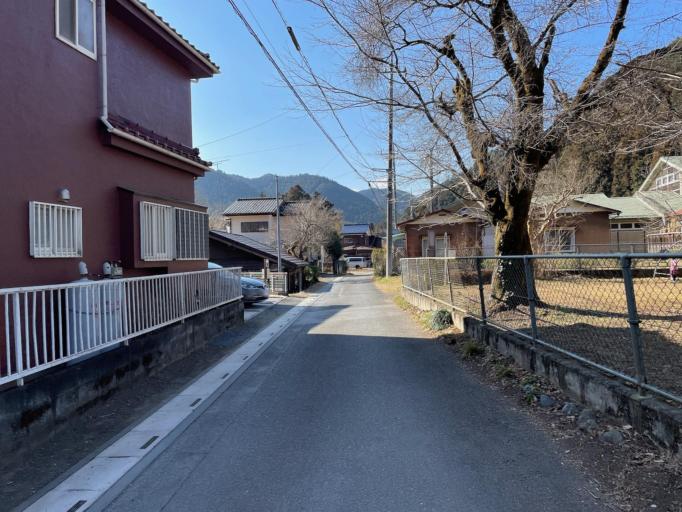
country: JP
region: Tokyo
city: Ome
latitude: 35.8652
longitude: 139.2370
